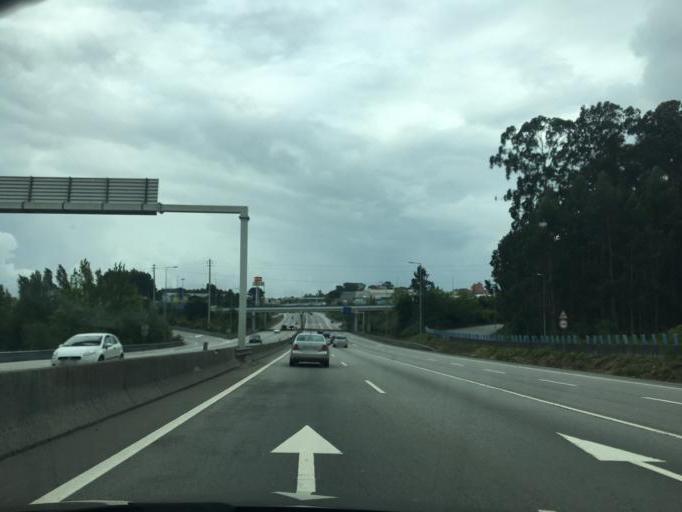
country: PT
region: Porto
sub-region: Maia
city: Leca do Bailio
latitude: 41.2049
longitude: -8.6274
